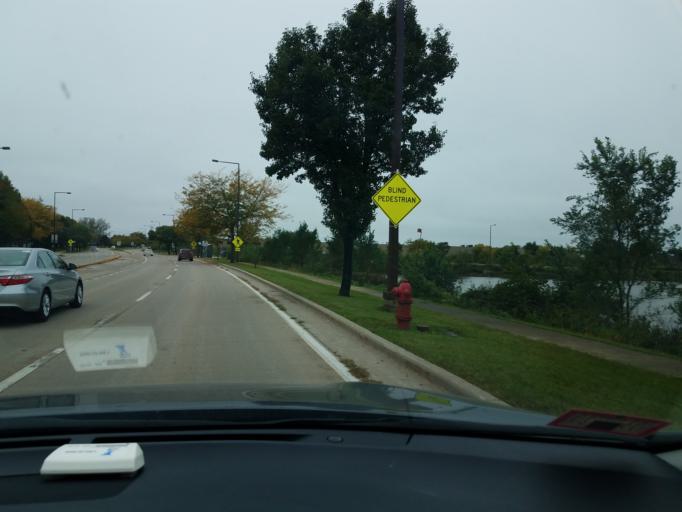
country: US
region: Illinois
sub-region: Cook County
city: Wheeling
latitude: 42.1688
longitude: -87.9307
